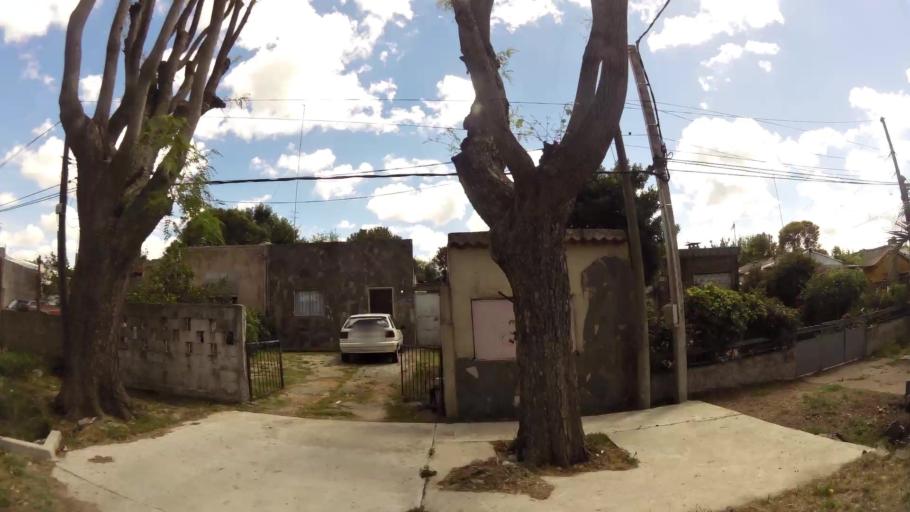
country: UY
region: Canelones
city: Paso de Carrasco
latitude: -34.8375
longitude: -56.1147
